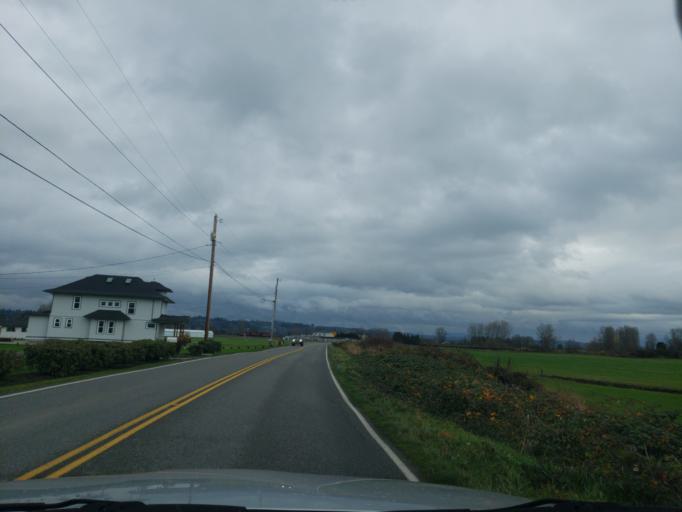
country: US
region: Washington
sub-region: Snohomish County
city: Snohomish
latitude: 47.9007
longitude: -122.1056
